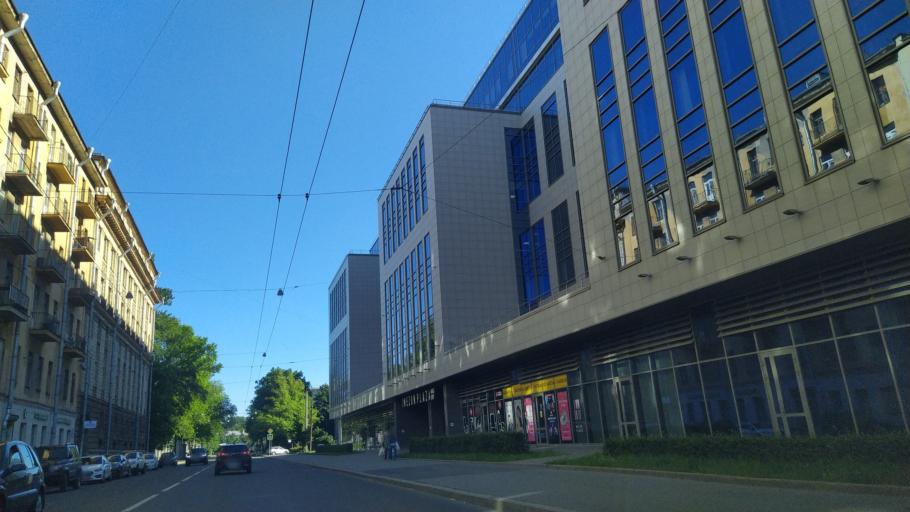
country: RU
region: Leningrad
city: Sampsonievskiy
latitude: 59.9644
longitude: 30.3437
